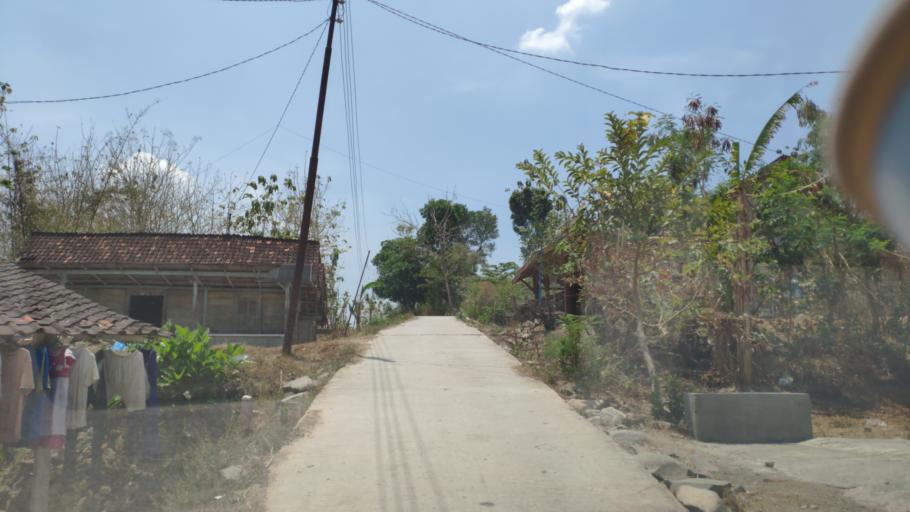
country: ID
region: Central Java
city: Singonegoro
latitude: -6.9706
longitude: 111.5240
